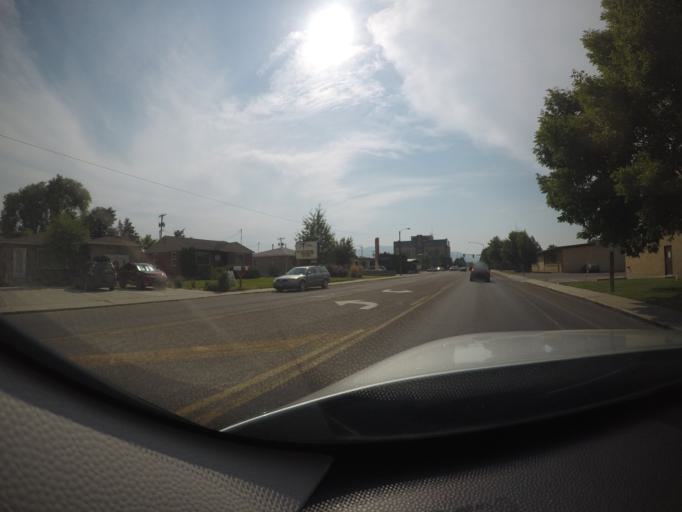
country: US
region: Montana
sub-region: Missoula County
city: Orchard Homes
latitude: 46.8489
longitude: -114.0225
